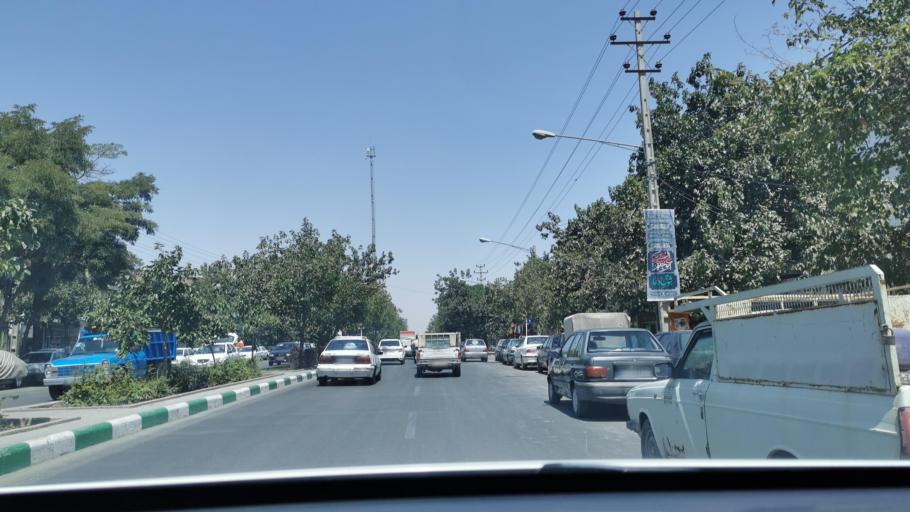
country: IR
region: Razavi Khorasan
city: Mashhad
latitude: 36.3425
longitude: 59.6254
